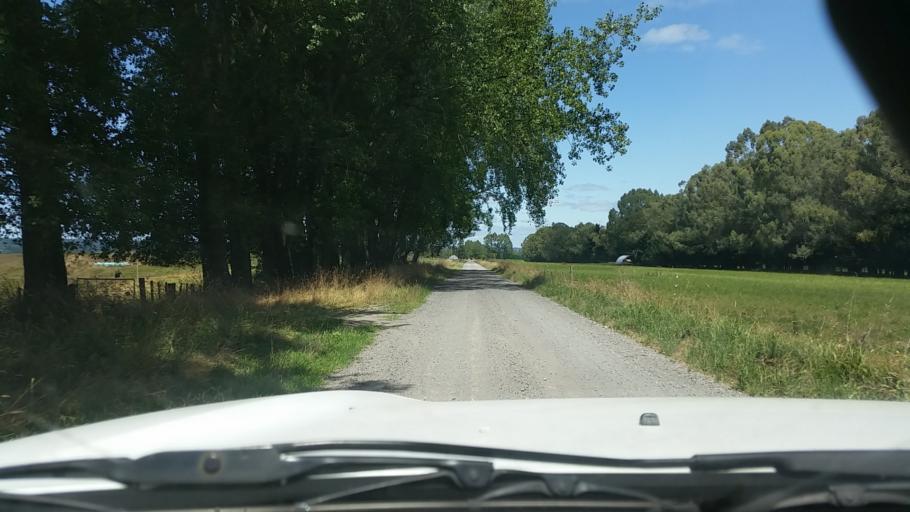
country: NZ
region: Bay of Plenty
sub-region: Whakatane District
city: Murupara
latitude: -38.4714
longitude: 176.4167
